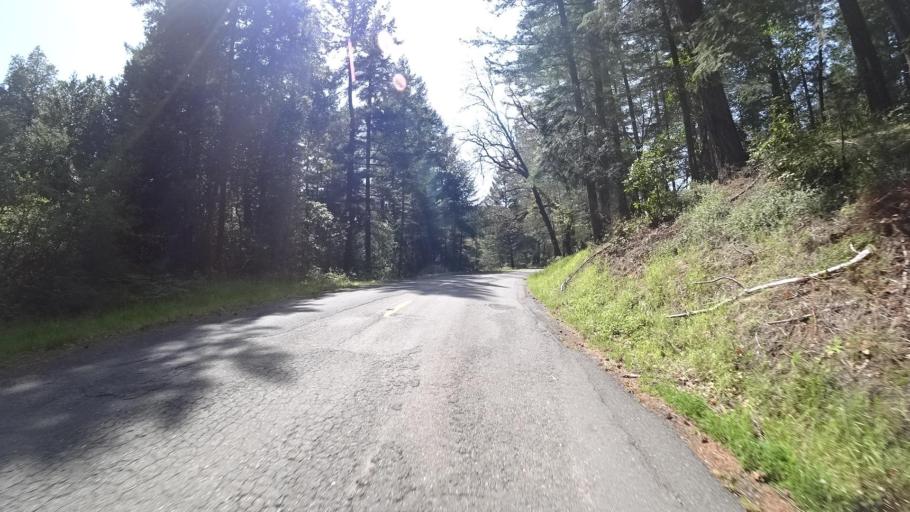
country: US
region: California
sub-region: Humboldt County
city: Redway
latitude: 40.3348
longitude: -123.6843
